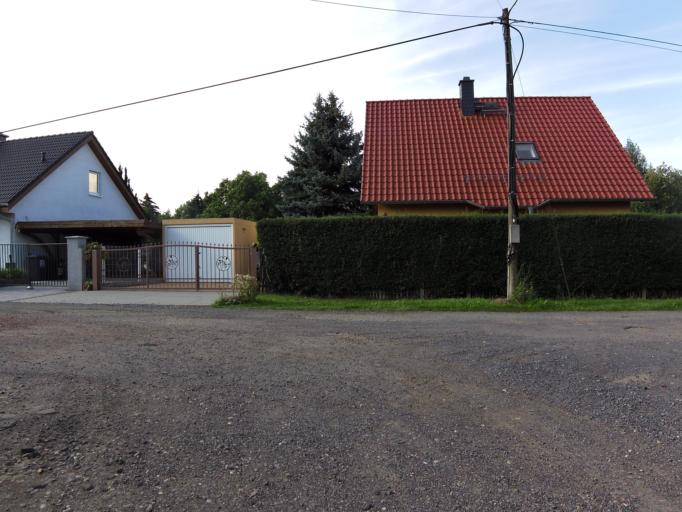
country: DE
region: Saxony
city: Taucha
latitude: 51.3485
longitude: 12.4651
